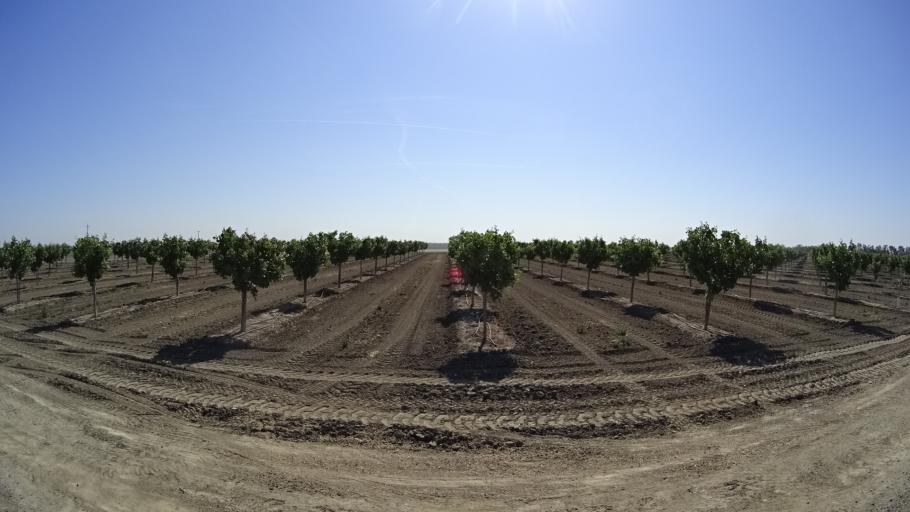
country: US
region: California
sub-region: Fresno County
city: Riverdale
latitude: 36.3851
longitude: -119.9413
